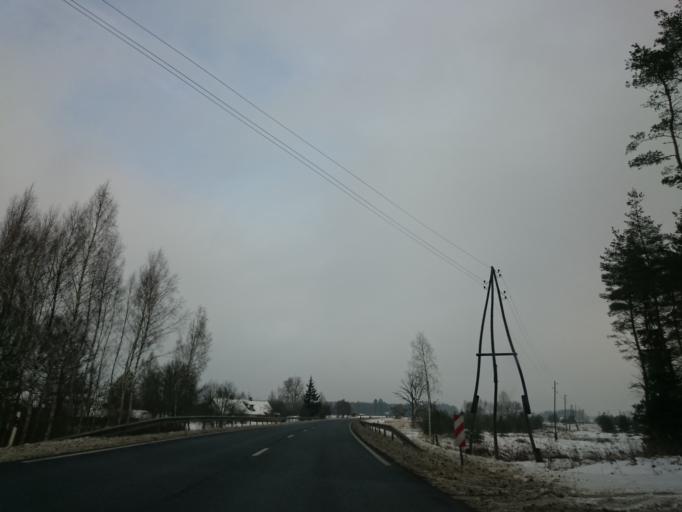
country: LV
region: Pargaujas
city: Stalbe
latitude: 57.3298
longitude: 24.9228
